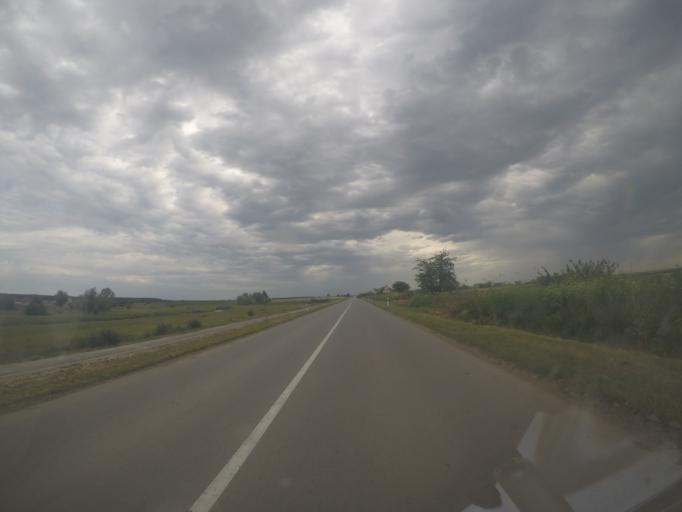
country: RS
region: Autonomna Pokrajina Vojvodina
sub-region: Juznobanatski Okrug
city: Opovo
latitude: 45.0616
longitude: 20.4359
